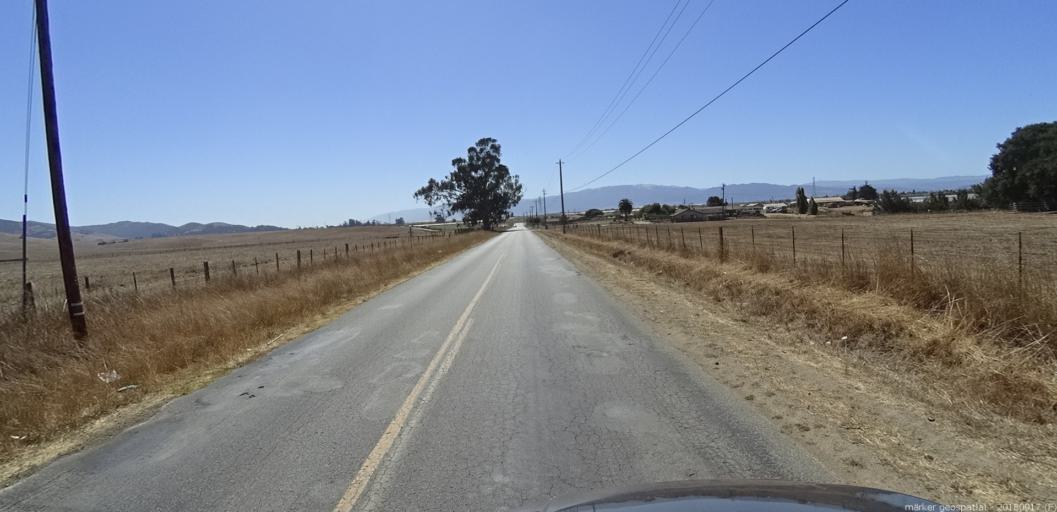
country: US
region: California
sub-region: Monterey County
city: Salinas
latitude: 36.7247
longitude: -121.5941
